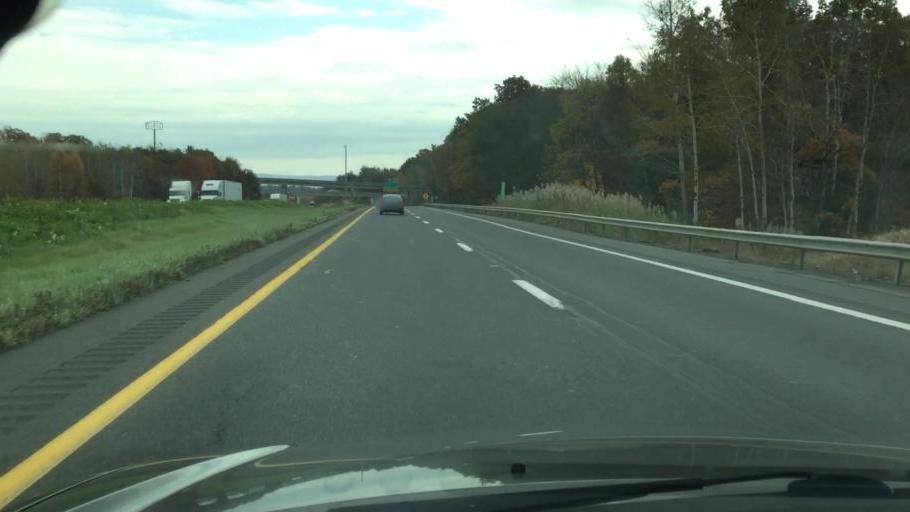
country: US
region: Pennsylvania
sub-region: Monroe County
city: Tannersville
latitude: 40.9995
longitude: -75.2734
